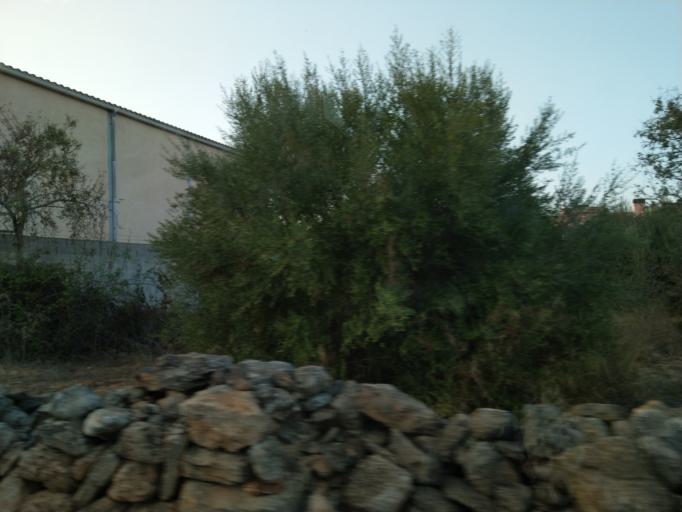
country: ES
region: Balearic Islands
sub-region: Illes Balears
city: Ses Salines
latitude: 39.3404
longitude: 3.0618
